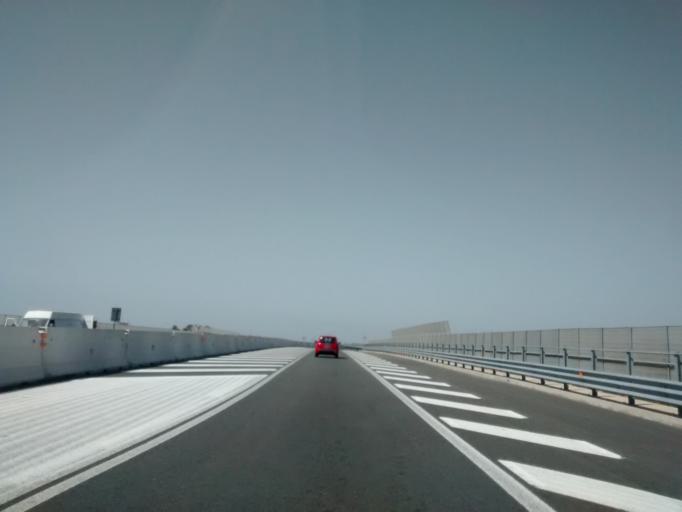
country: IT
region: Sardinia
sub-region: Provincia di Cagliari
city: Quartu Sant'Elena
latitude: 39.2587
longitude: 9.2603
